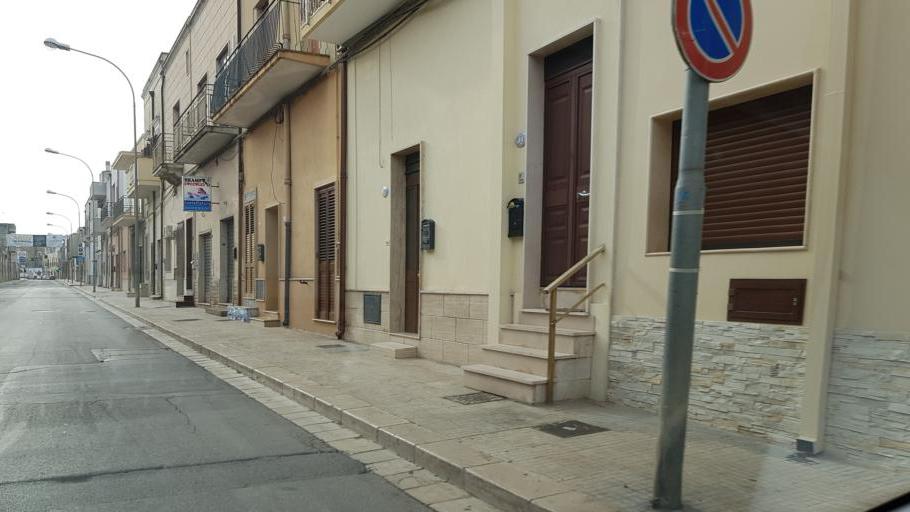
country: IT
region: Apulia
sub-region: Provincia di Brindisi
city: Mesagne
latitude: 40.5630
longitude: 17.8118
